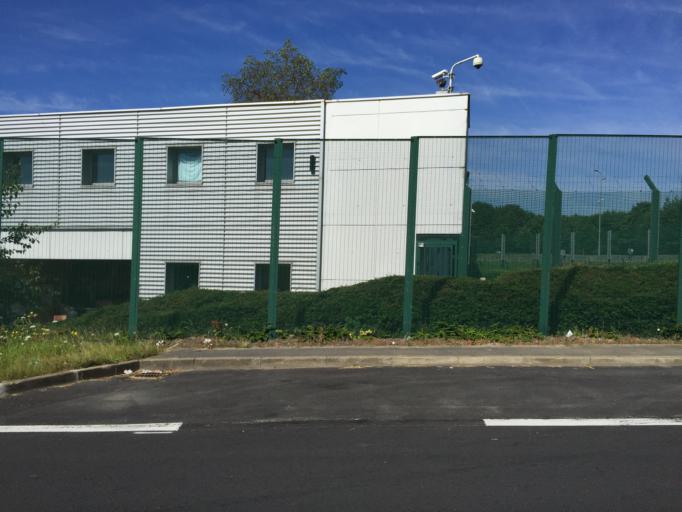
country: FR
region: Ile-de-France
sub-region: Departement du Val-d'Oise
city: Roissy-en-France
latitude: 49.0059
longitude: 2.5516
